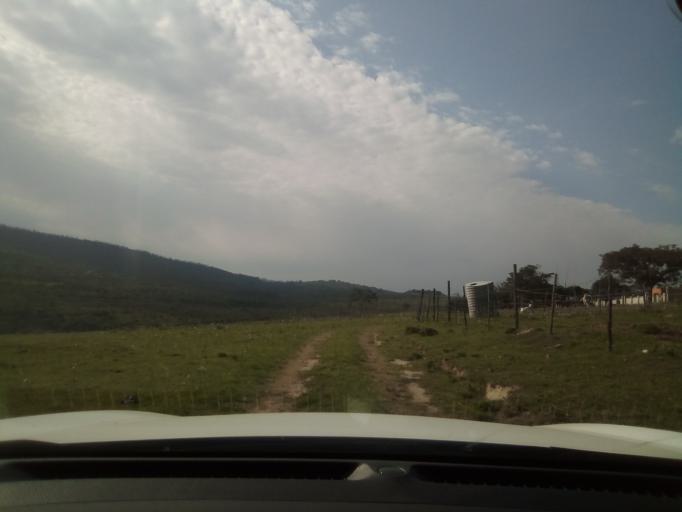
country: ZA
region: Eastern Cape
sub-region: Buffalo City Metropolitan Municipality
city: Bhisho
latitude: -32.9814
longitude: 27.2577
